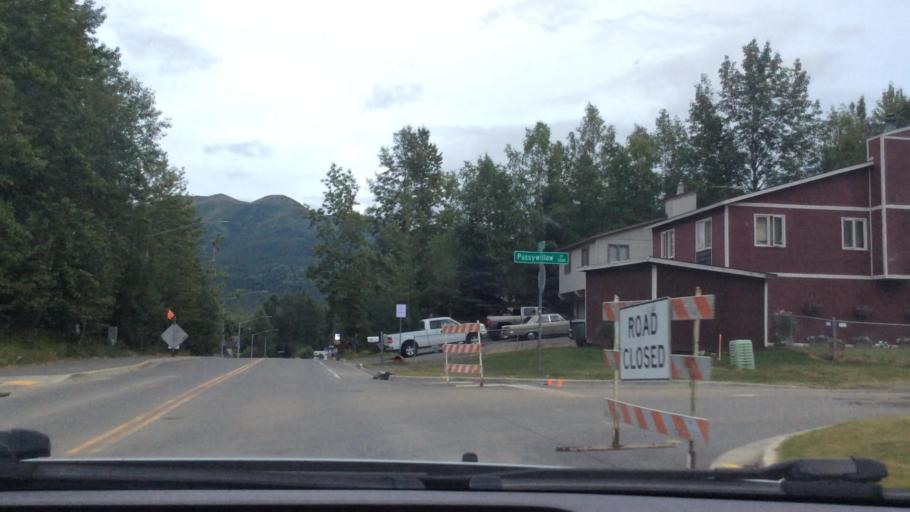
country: US
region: Alaska
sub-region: Anchorage Municipality
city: Elmendorf Air Force Base
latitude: 61.1919
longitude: -149.7262
